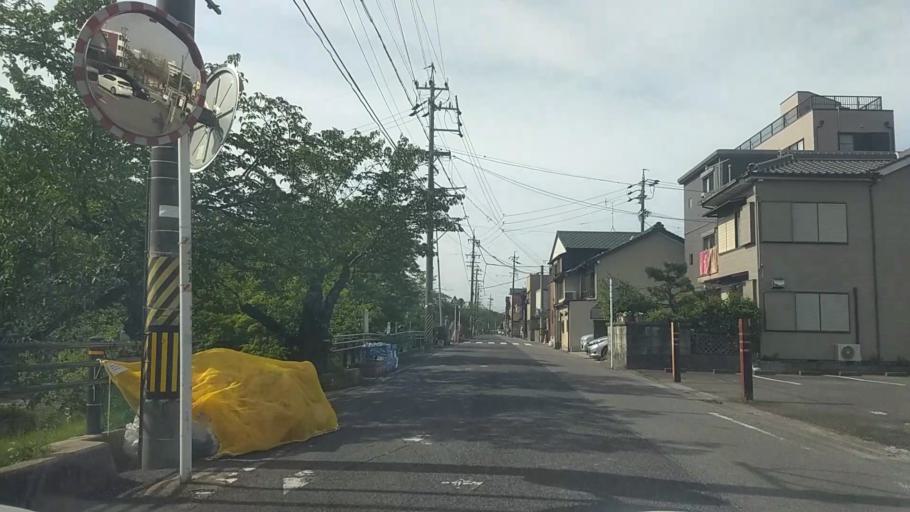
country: JP
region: Aichi
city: Okazaki
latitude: 34.9577
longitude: 137.1578
